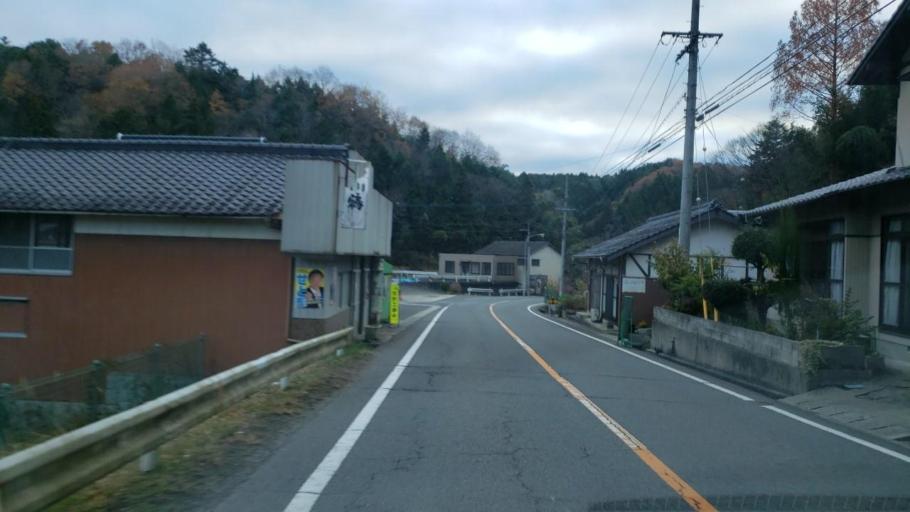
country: JP
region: Tokushima
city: Wakimachi
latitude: 34.1900
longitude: 134.1742
